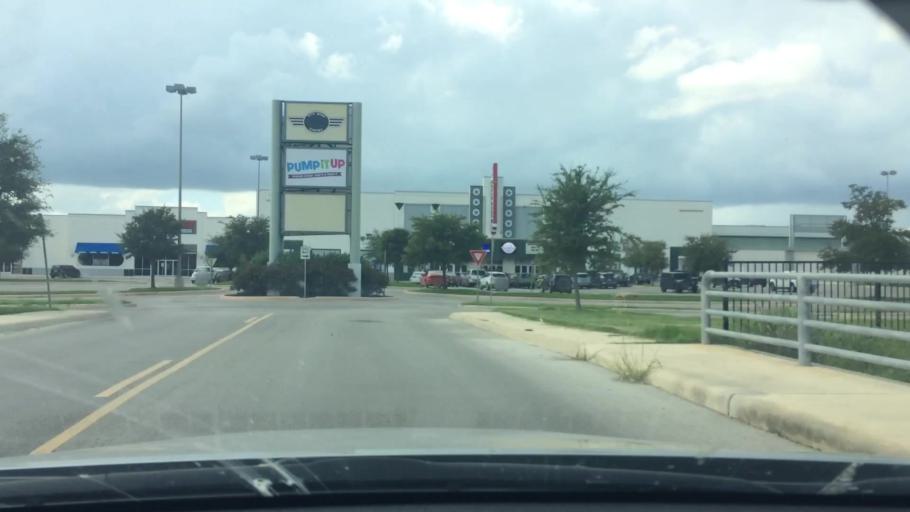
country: US
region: Texas
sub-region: Bexar County
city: San Antonio
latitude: 29.3540
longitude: -98.4500
